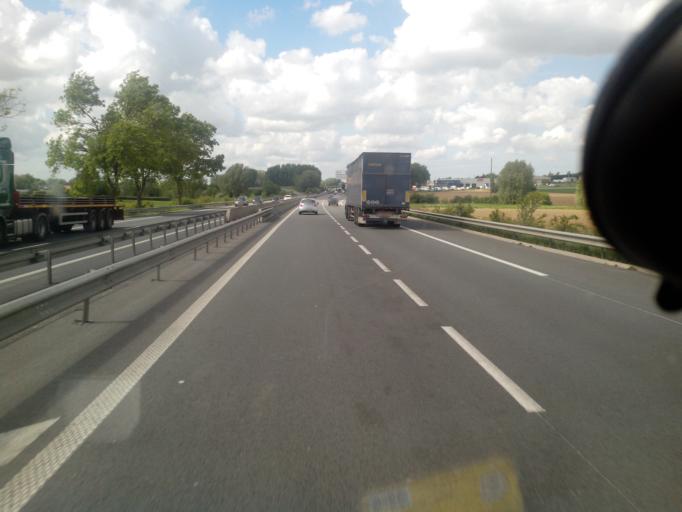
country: FR
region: Nord-Pas-de-Calais
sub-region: Departement du Nord
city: Steenvoorde
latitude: 50.8031
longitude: 2.6035
